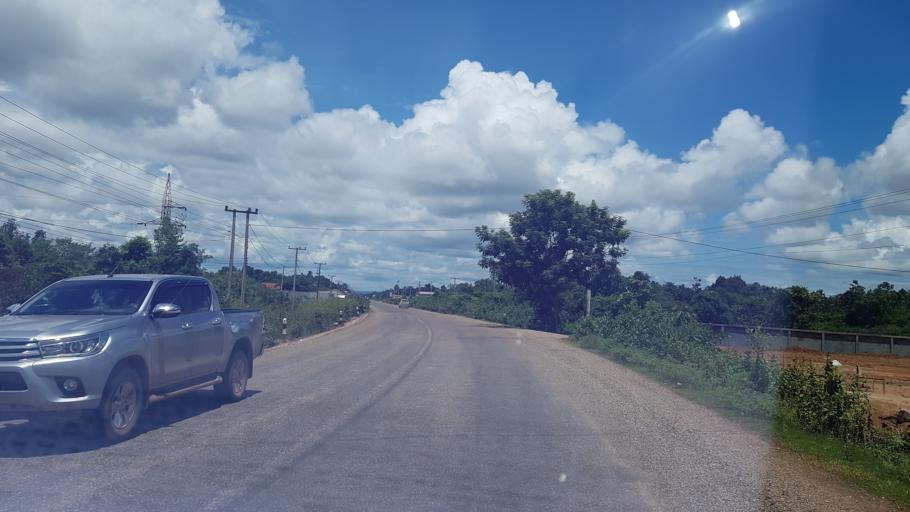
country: LA
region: Vientiane
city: Vientiane
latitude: 18.1072
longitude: 102.5705
